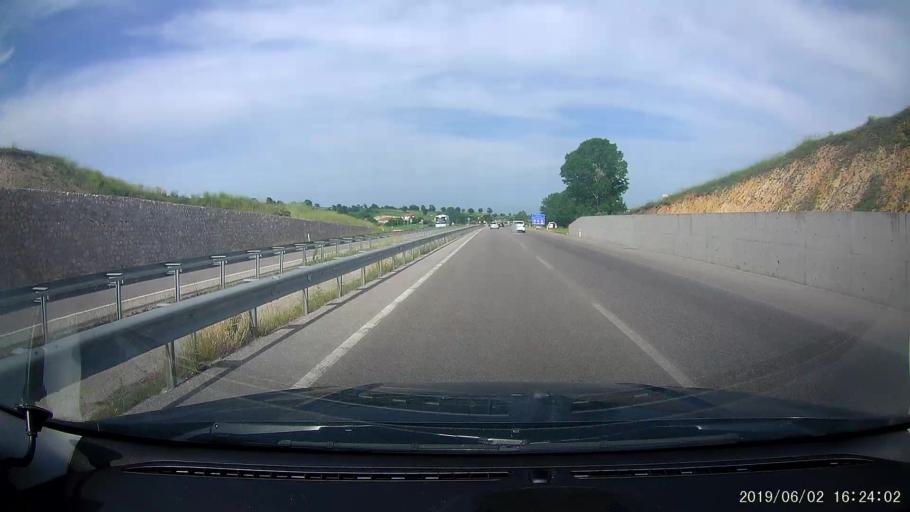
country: TR
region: Samsun
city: Havza
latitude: 40.9968
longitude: 35.7495
